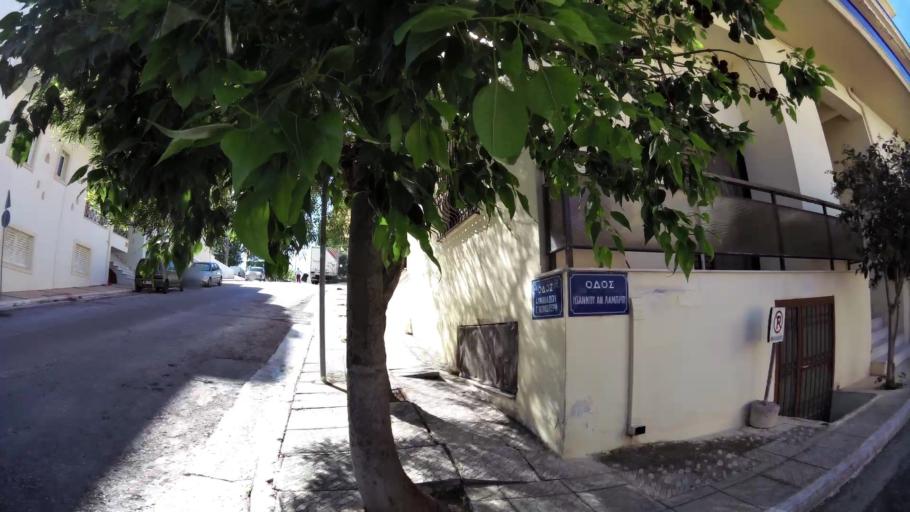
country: GR
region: Attica
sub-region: Nomarchia Anatolikis Attikis
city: Koropi
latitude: 37.9030
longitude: 23.8765
